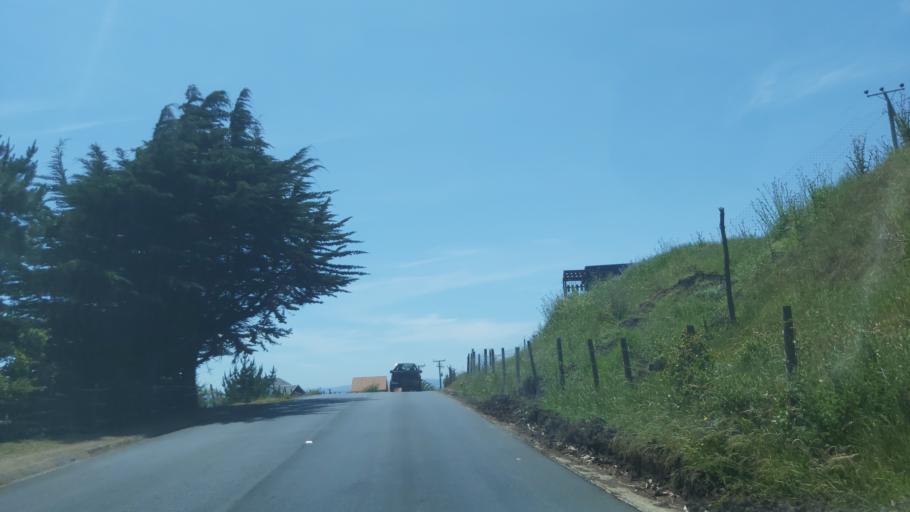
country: CL
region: Maule
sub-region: Provincia de Cauquenes
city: Cauquenes
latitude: -35.8279
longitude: -72.6143
